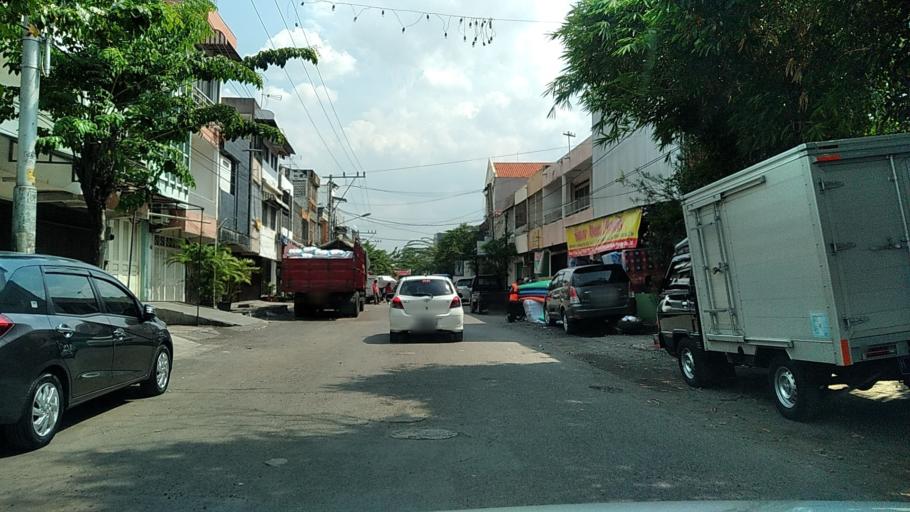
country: ID
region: Central Java
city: Semarang
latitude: -6.9759
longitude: 110.4251
